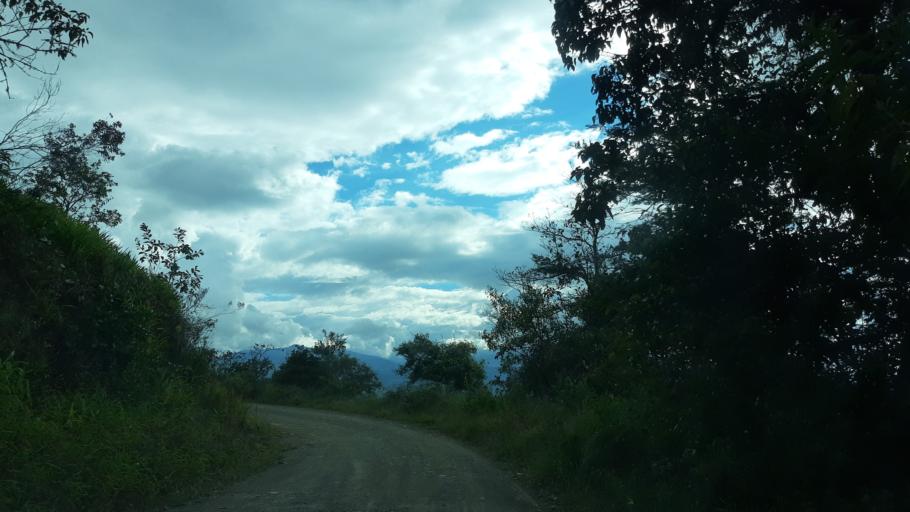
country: CO
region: Boyaca
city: Garagoa
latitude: 5.0053
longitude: -73.3400
